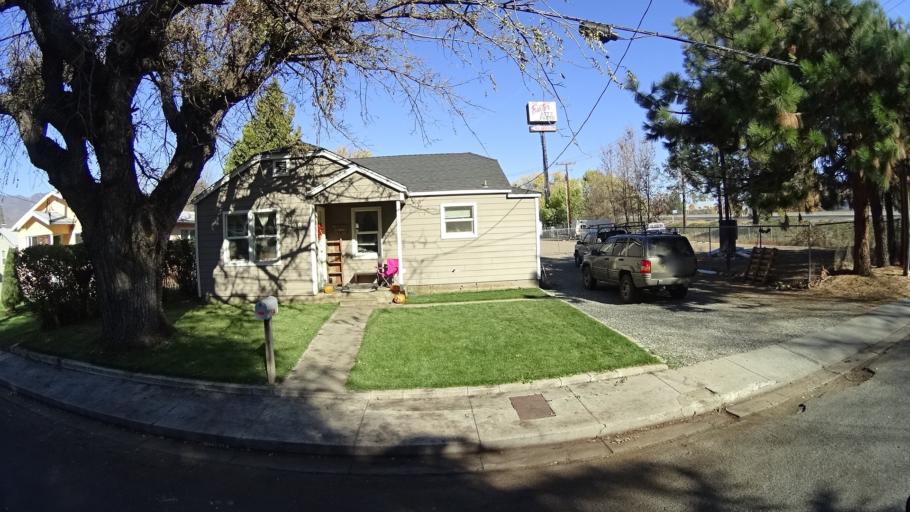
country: US
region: California
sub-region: Siskiyou County
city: Yreka
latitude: 41.7285
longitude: -122.6348
